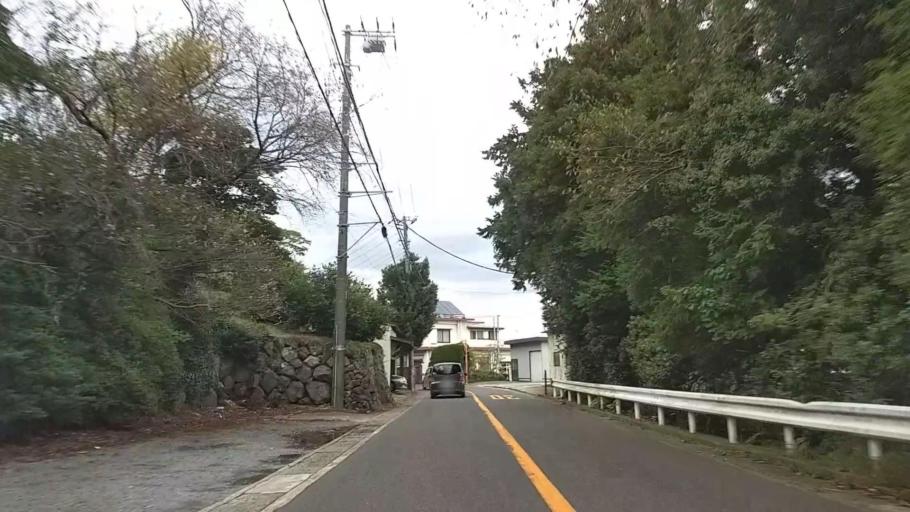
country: JP
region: Kanagawa
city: Odawara
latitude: 35.1900
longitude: 139.1333
